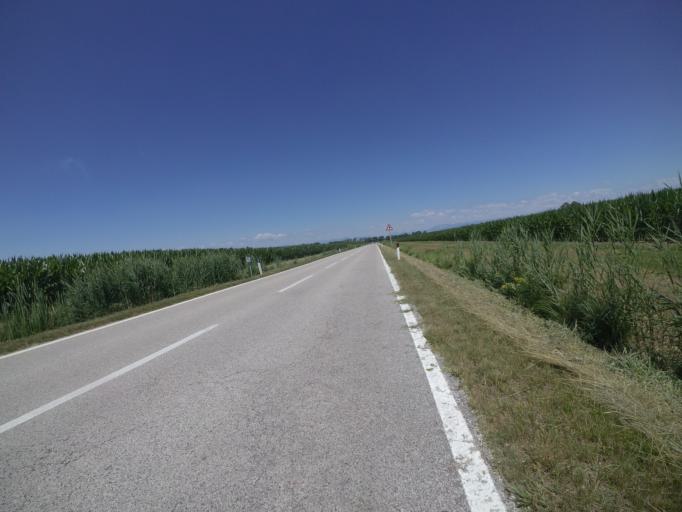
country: IT
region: Friuli Venezia Giulia
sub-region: Provincia di Udine
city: Rivignano
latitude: 45.9025
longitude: 13.0815
